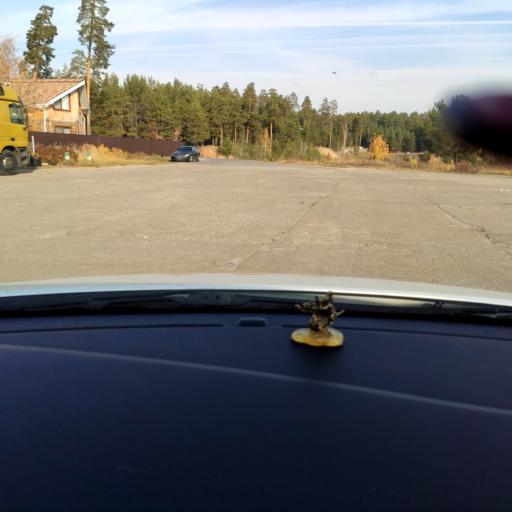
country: RU
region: Tatarstan
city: Staroye Arakchino
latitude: 55.8230
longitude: 48.9181
